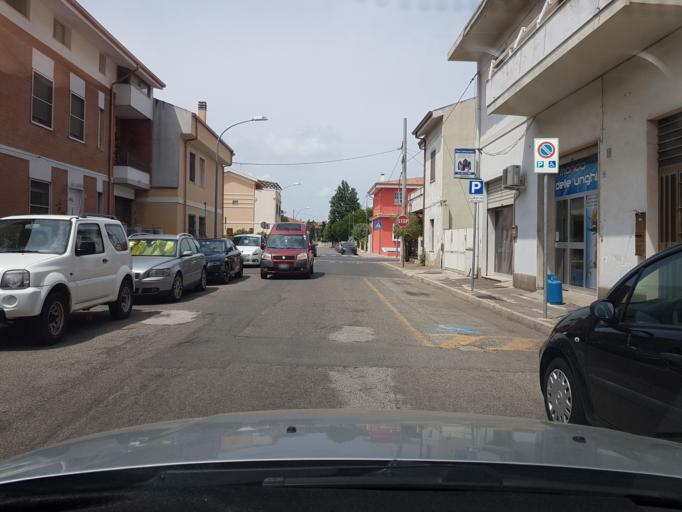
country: IT
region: Sardinia
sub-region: Provincia di Oristano
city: Oristano
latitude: 39.9109
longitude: 8.5930
